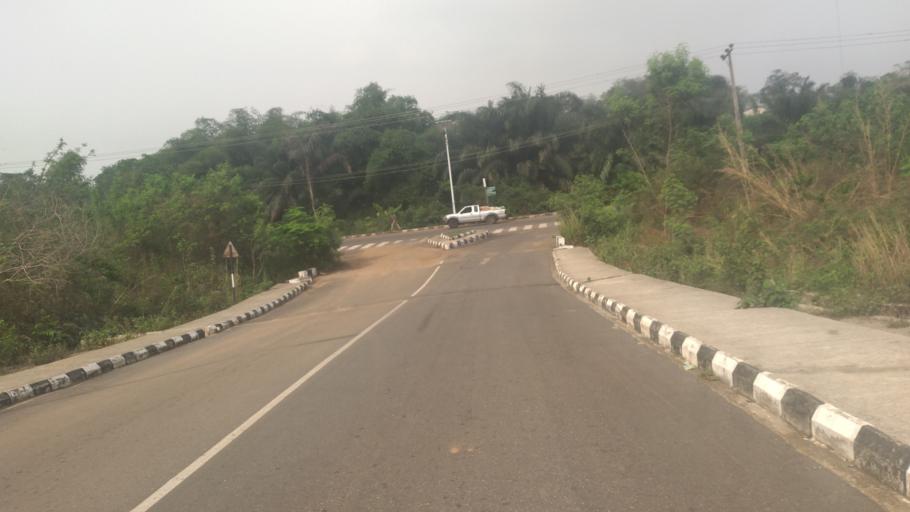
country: NG
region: Ondo
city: Ilare
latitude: 7.2979
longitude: 5.1429
